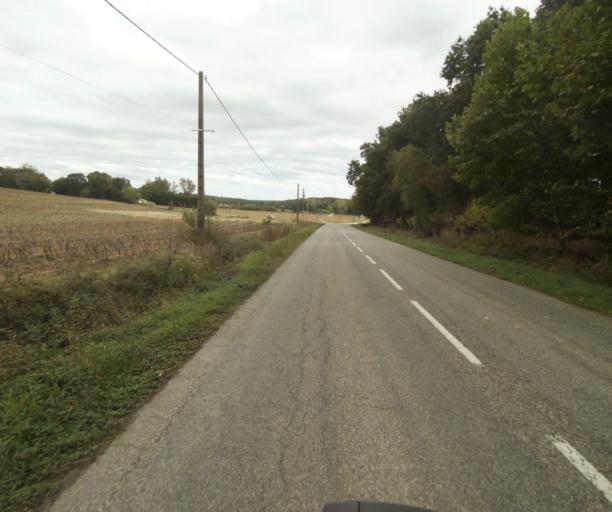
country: FR
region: Midi-Pyrenees
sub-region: Departement du Tarn-et-Garonne
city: Verdun-sur-Garonne
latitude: 43.8570
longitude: 1.1244
